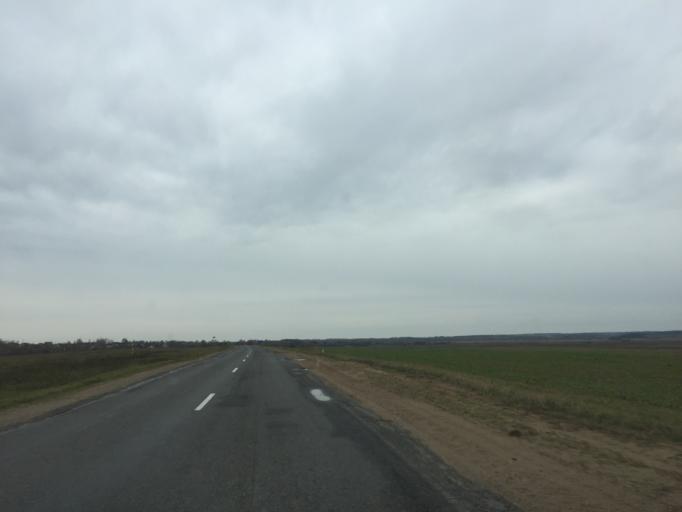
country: BY
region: Mogilev
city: Drybin
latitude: 54.1410
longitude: 31.1138
